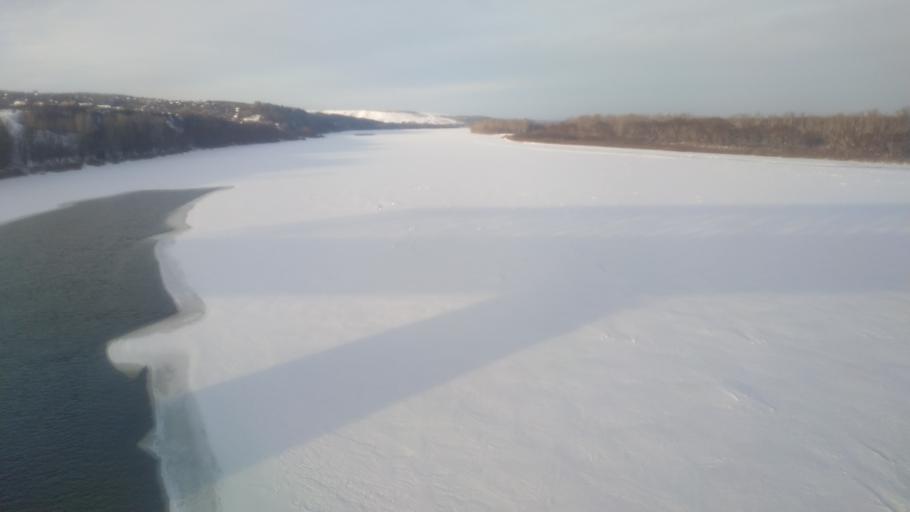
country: RU
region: Kirov
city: Vyatskiye Polyany
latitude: 56.2537
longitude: 51.0686
